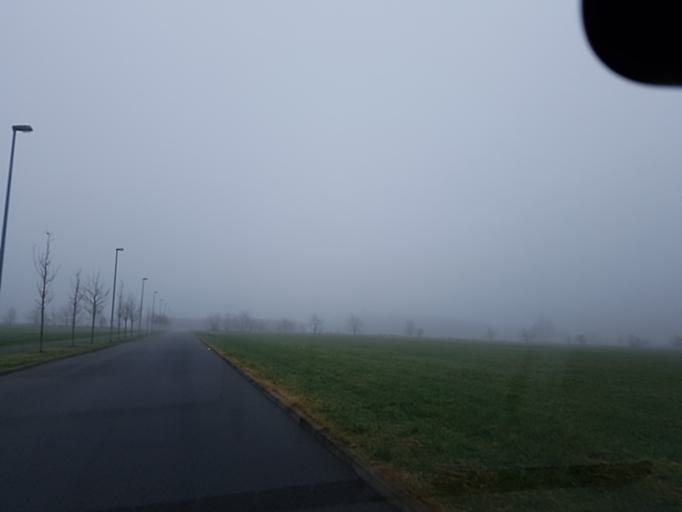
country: DE
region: Brandenburg
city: Finsterwalde
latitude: 51.6308
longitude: 13.7385
